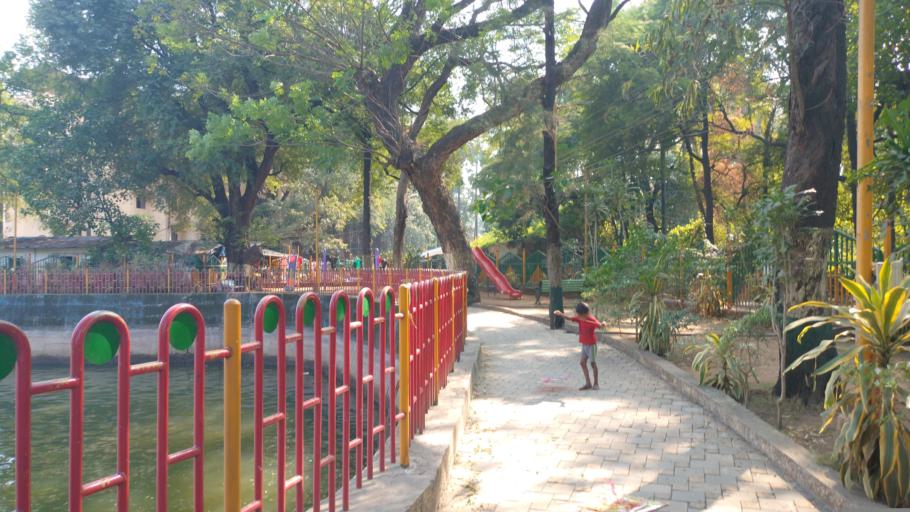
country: IN
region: Maharashtra
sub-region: Thane
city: Virar
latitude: 19.4507
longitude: 72.7935
